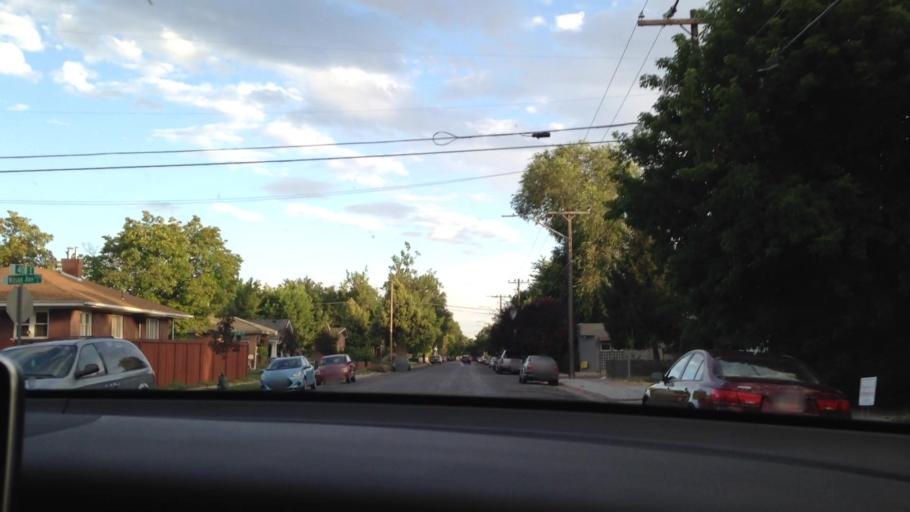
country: US
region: Utah
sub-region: Salt Lake County
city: South Salt Lake
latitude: 40.7321
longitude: -111.8797
